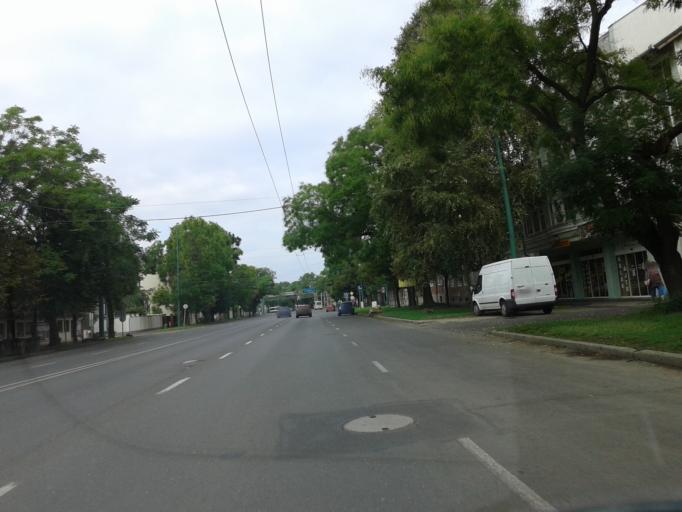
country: HU
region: Csongrad
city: Szeged
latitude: 46.2616
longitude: 20.1545
